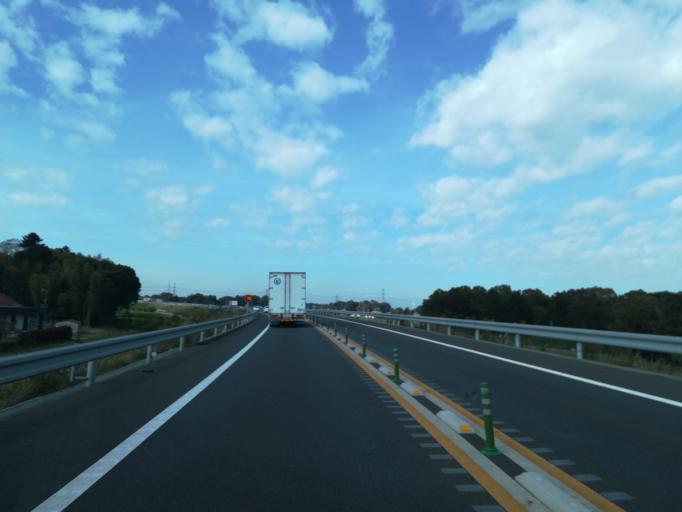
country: JP
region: Ibaraki
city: Sakai
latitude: 36.1098
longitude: 139.8585
